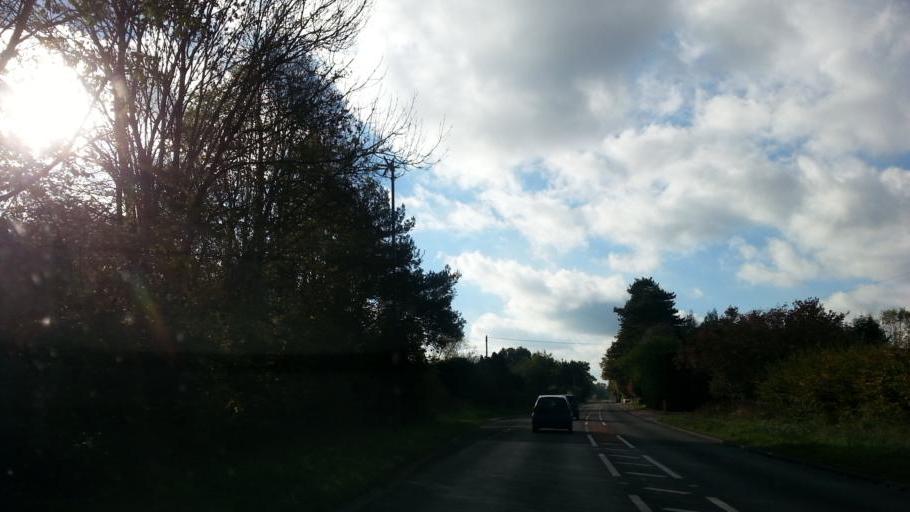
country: GB
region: England
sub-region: Norfolk
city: Ditchingham
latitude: 52.4825
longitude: 1.4870
